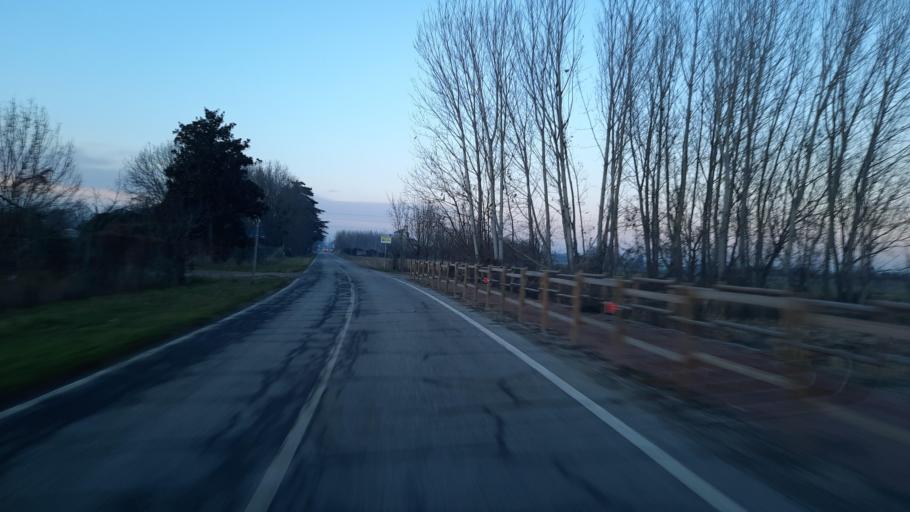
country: IT
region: Piedmont
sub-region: Provincia di Vercelli
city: Trino
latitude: 45.1797
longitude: 8.2955
